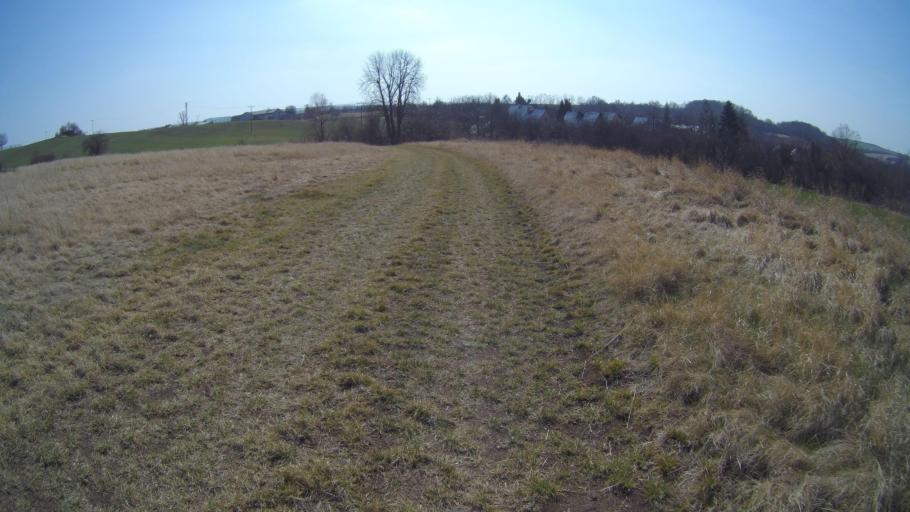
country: CZ
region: Ustecky
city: Mecholupy
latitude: 50.2645
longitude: 13.5471
